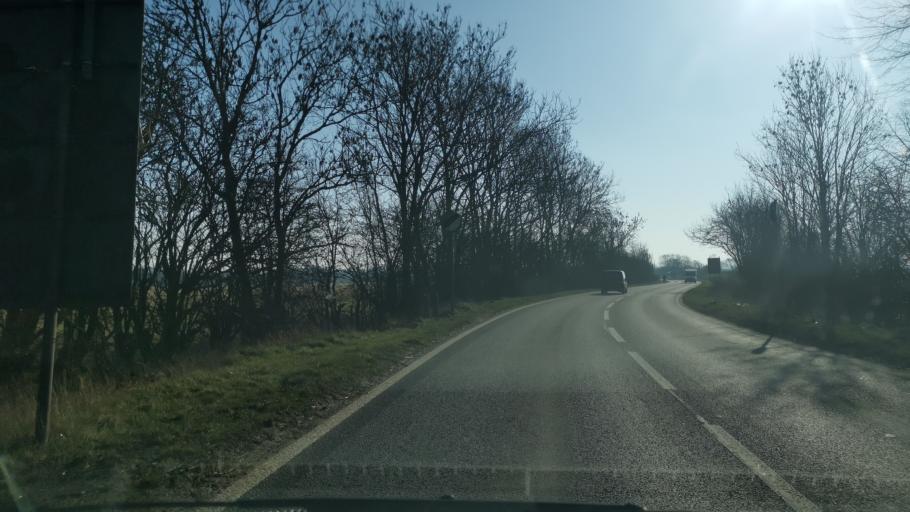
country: GB
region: England
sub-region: City of York
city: Wigginton
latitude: 53.9883
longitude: -1.0856
